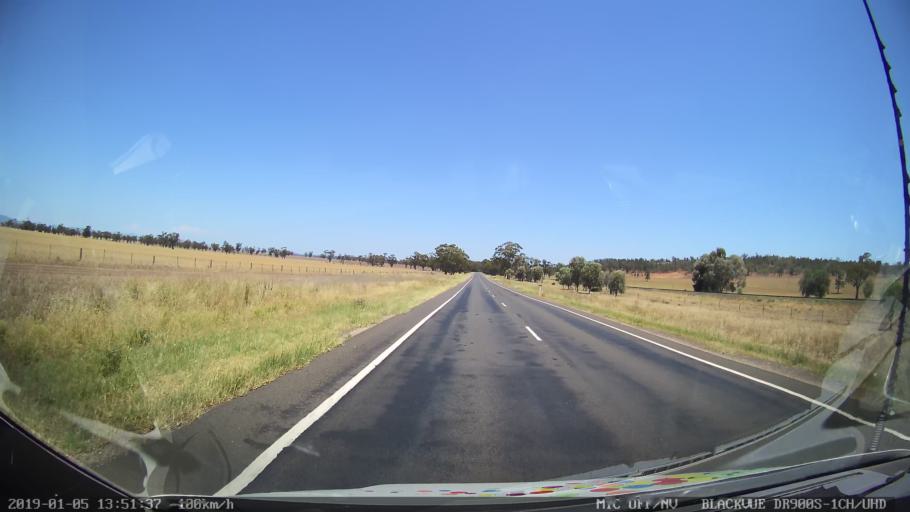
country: AU
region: New South Wales
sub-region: Gunnedah
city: Gunnedah
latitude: -31.0473
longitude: 150.2771
